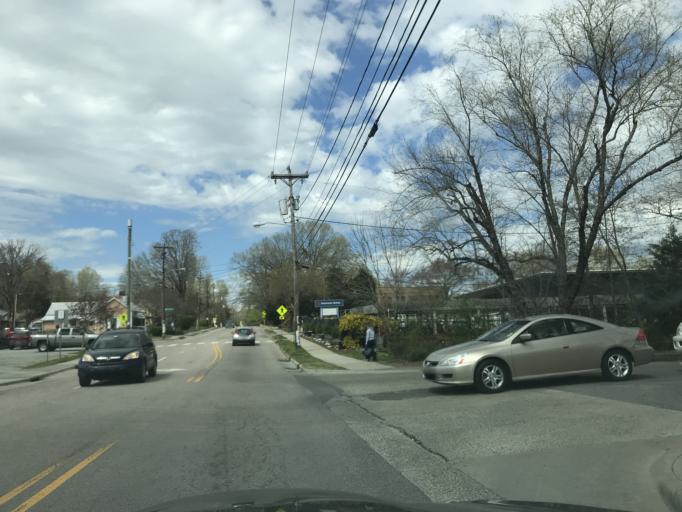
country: US
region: North Carolina
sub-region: Orange County
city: Carrboro
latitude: 35.9124
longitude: -79.0722
